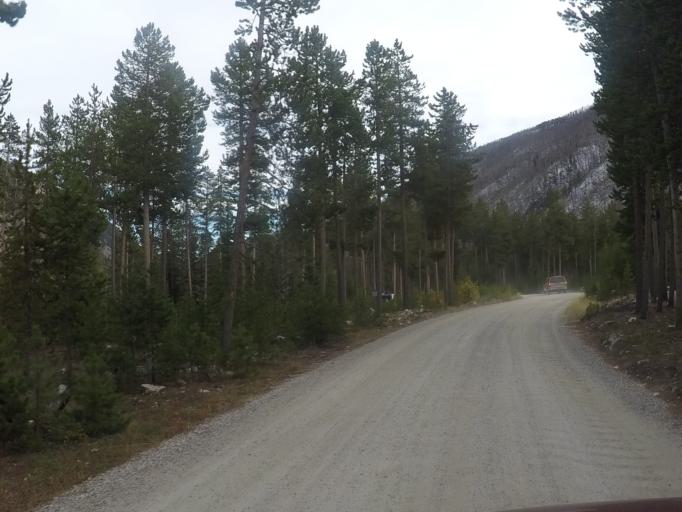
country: US
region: Montana
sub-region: Carbon County
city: Red Lodge
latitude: 45.1681
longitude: -109.4090
